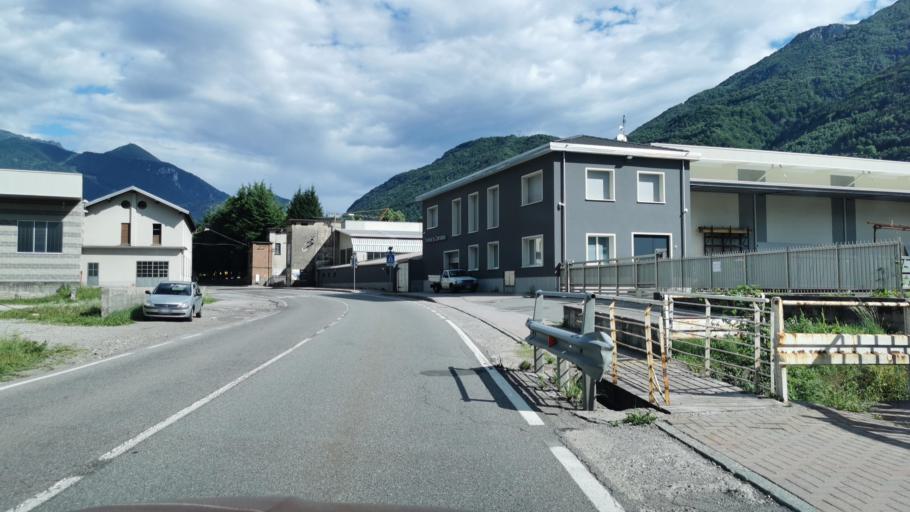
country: IT
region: Lombardy
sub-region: Provincia di Lecco
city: Primaluna
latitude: 45.9908
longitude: 9.4130
